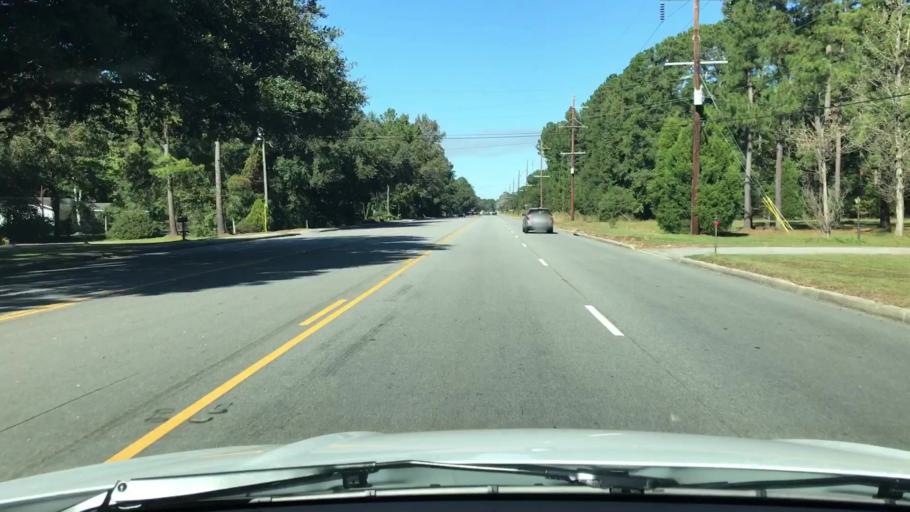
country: US
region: South Carolina
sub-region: Beaufort County
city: Laurel Bay
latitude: 32.5682
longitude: -80.7435
